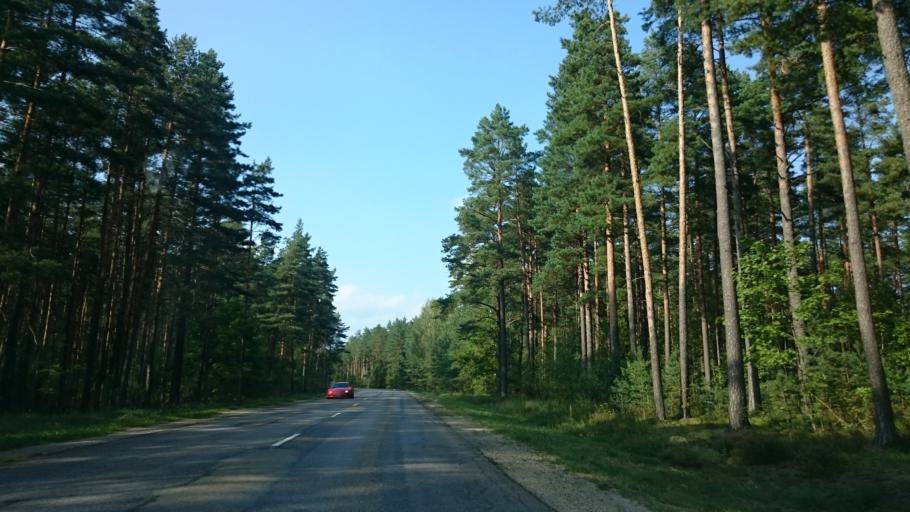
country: LV
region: Stopini
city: Ulbroka
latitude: 56.9557
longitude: 24.3099
